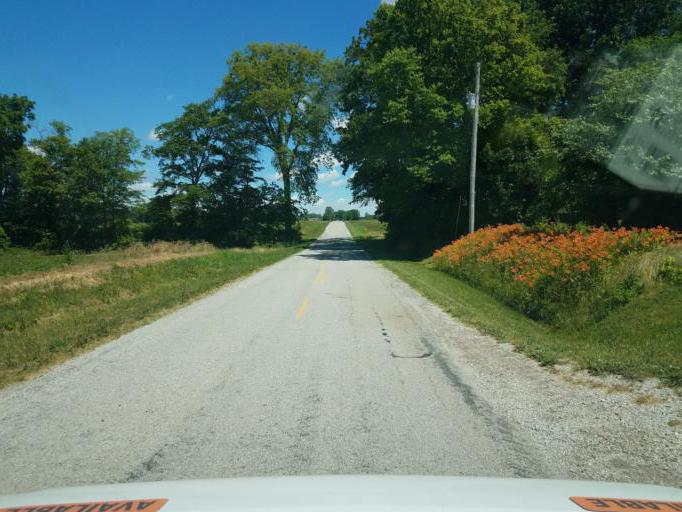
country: US
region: Ohio
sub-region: Crawford County
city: Bucyrus
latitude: 40.6596
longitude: -82.9387
